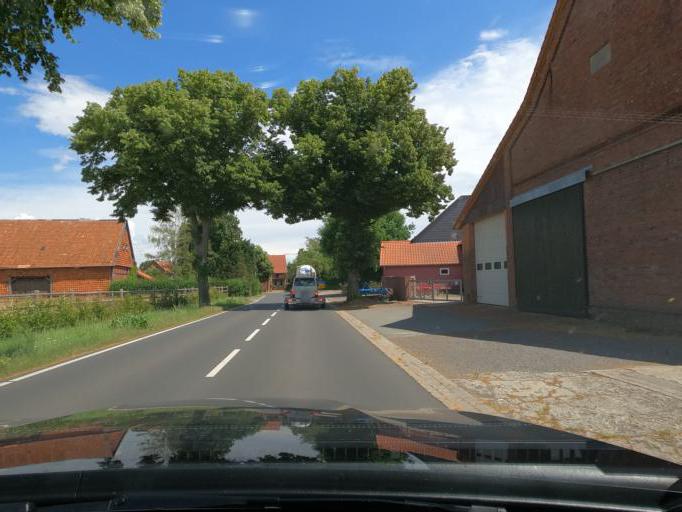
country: DE
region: Lower Saxony
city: Burgdorf
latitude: 52.1811
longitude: 10.1665
